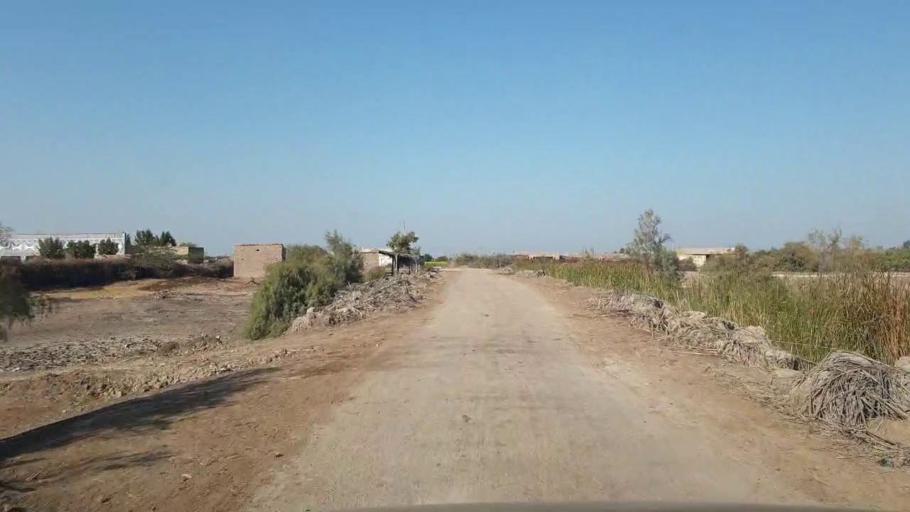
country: PK
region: Sindh
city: Shahpur Chakar
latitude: 26.1714
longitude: 68.6811
